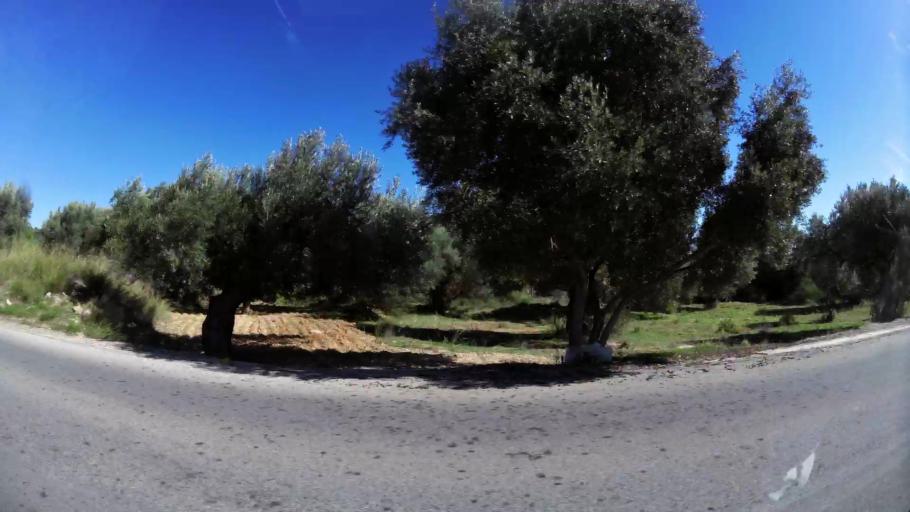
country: GR
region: Attica
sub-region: Nomarchia Anatolikis Attikis
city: Paiania
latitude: 37.9649
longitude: 23.8639
